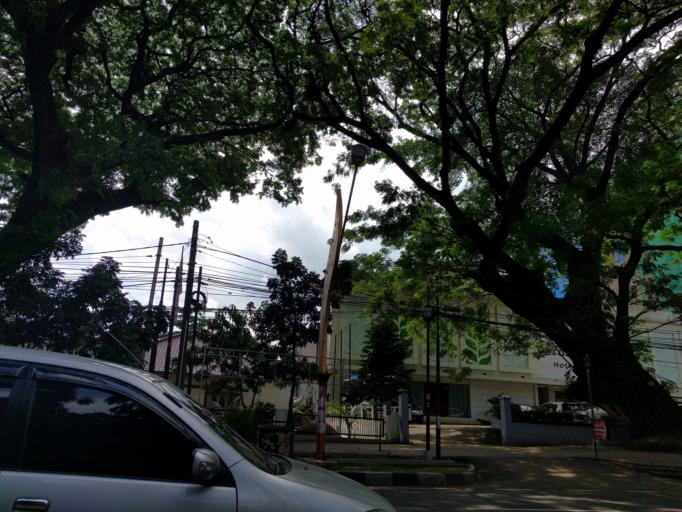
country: ID
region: West Java
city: Bogor
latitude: -6.5972
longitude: 106.8045
